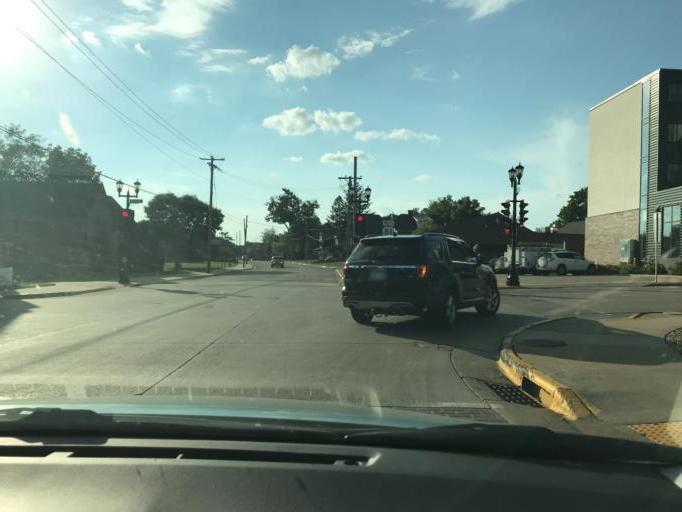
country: US
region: Wisconsin
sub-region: Grant County
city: Platteville
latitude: 42.7335
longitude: -90.4804
